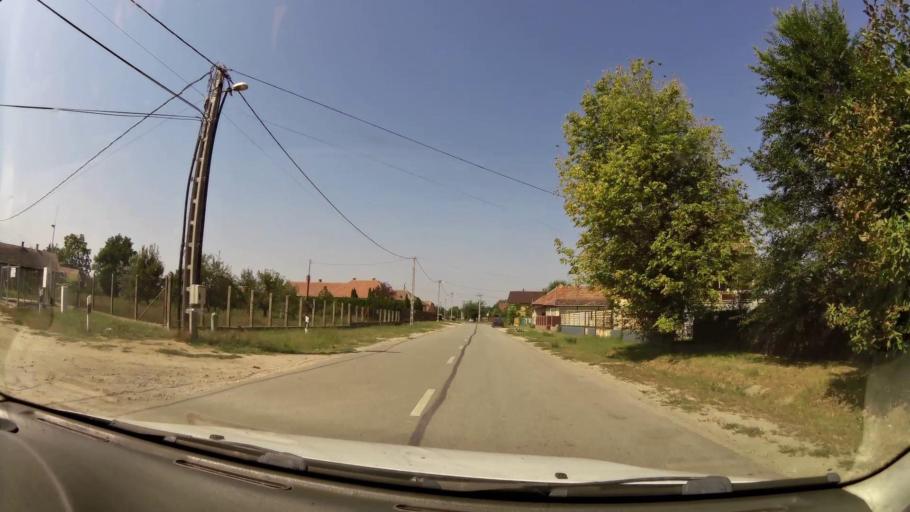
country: HU
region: Pest
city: Tapioszentmarton
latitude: 47.3431
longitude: 19.7766
